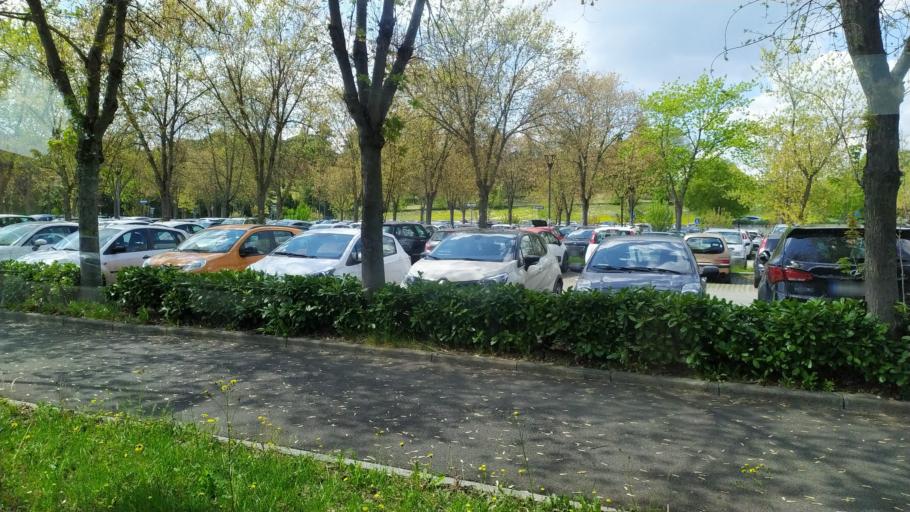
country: IT
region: Emilia-Romagna
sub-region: Provincia di Bologna
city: Imola
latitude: 44.3568
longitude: 11.6892
